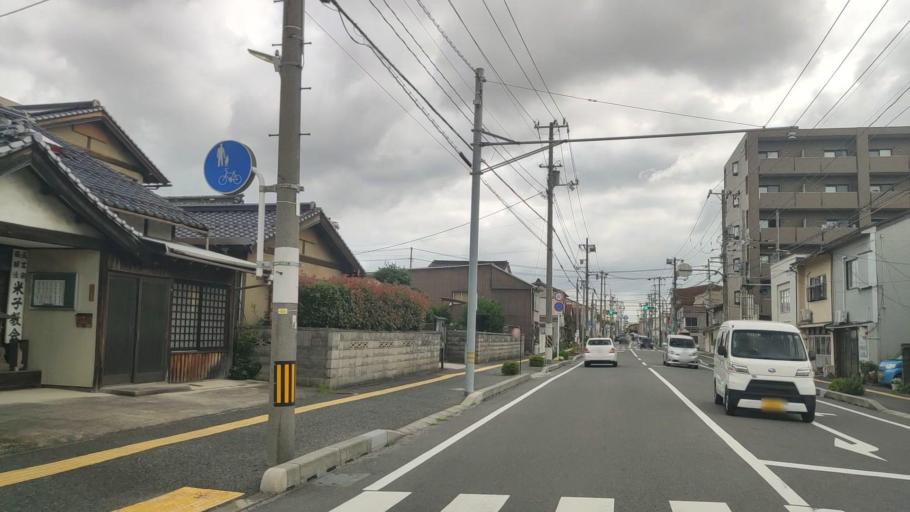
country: JP
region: Tottori
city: Yonago
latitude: 35.4293
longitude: 133.3354
